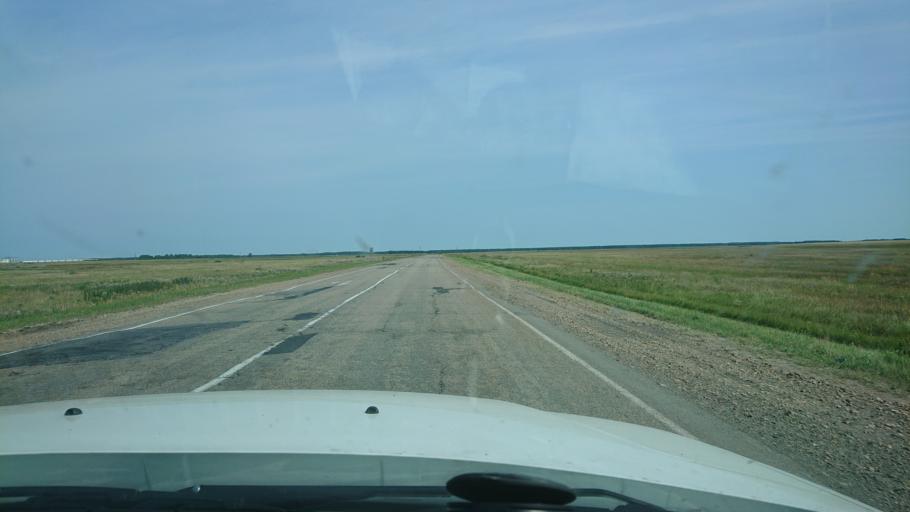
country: RU
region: Tjumen
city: Armizonskoye
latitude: 55.5374
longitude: 67.8985
